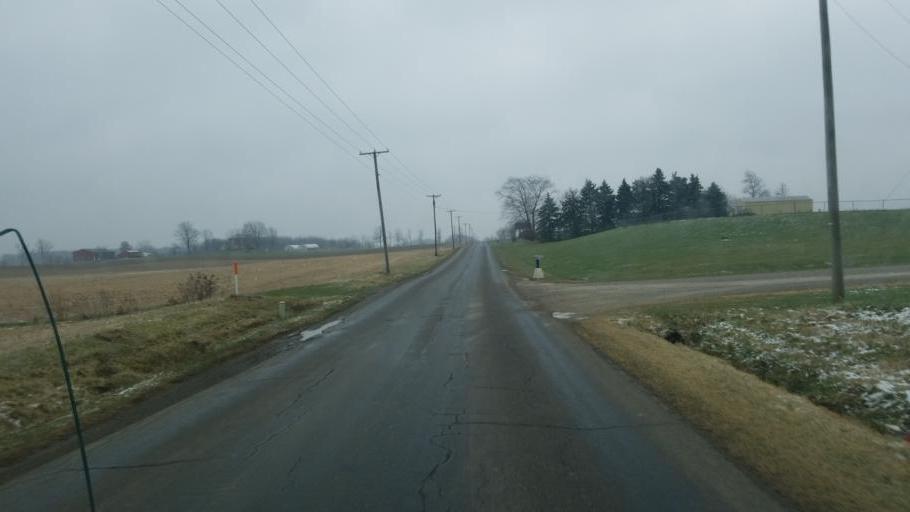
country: US
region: Ohio
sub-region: Huron County
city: Greenwich
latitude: 40.9752
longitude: -82.5707
